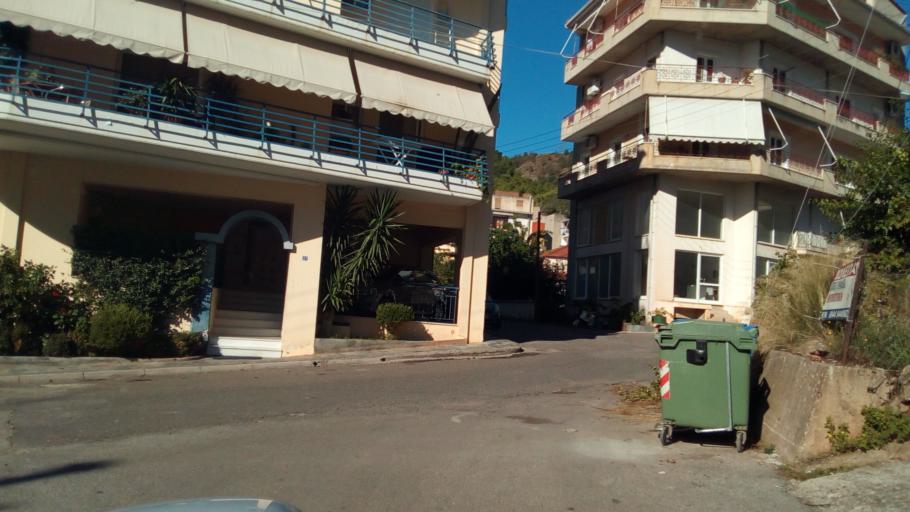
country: GR
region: West Greece
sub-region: Nomos Aitolias kai Akarnanias
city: Nafpaktos
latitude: 38.3968
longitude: 21.8328
